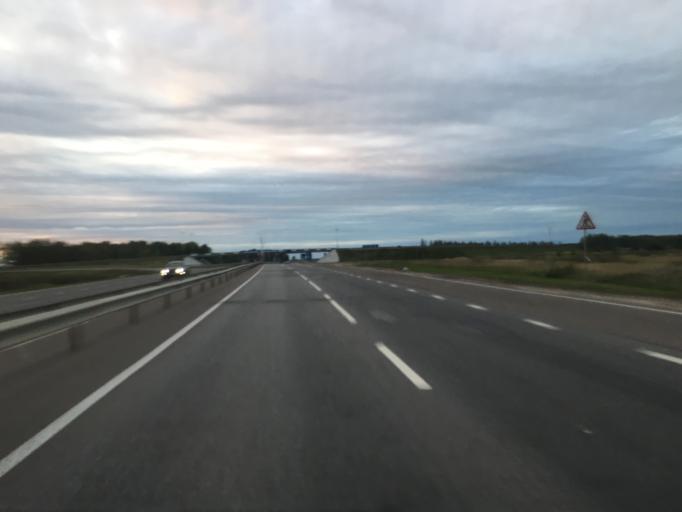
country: RU
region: Kaluga
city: Kaluga
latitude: 54.6221
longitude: 36.2922
